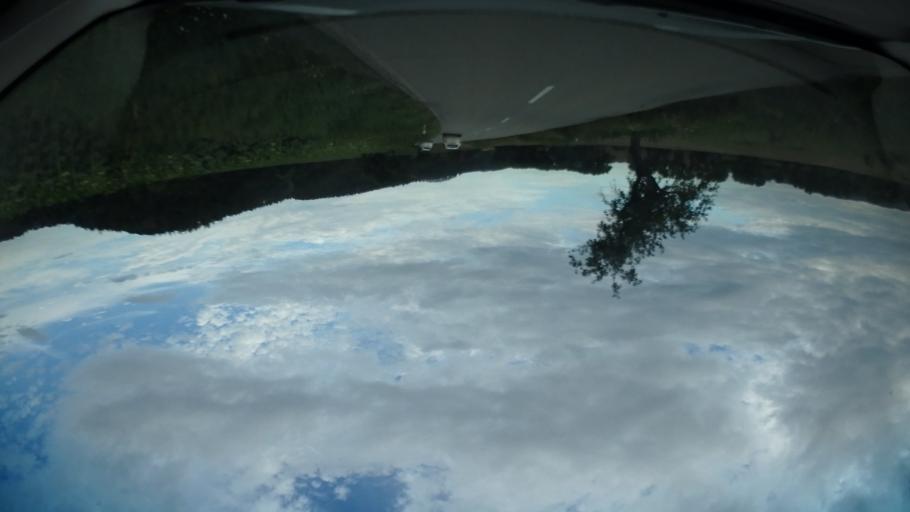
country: CZ
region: South Moravian
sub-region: Okres Blansko
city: Boskovice
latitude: 49.5106
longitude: 16.6730
